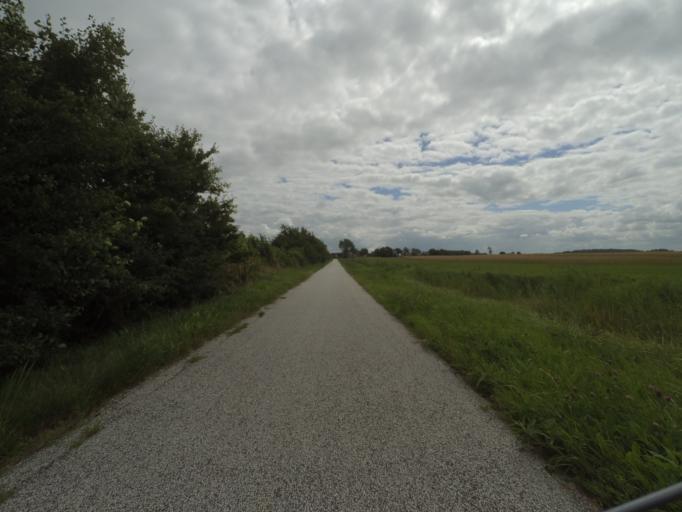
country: NL
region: Friesland
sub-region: Gemeente Kollumerland en Nieuwkruisland
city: Kollum
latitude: 53.3220
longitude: 6.1543
